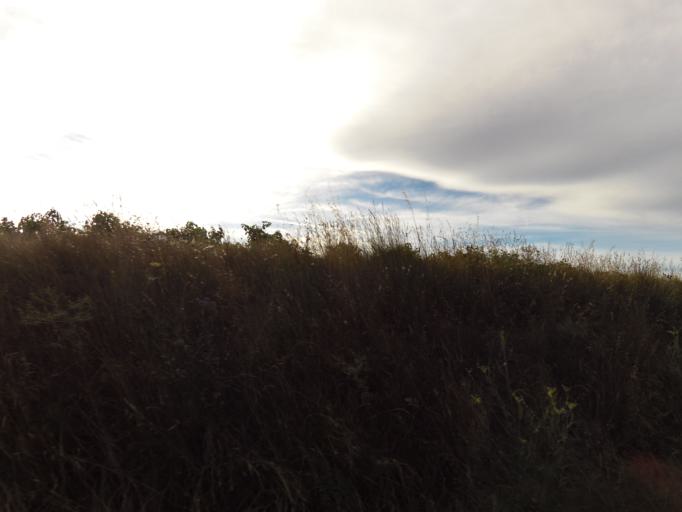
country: FR
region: Languedoc-Roussillon
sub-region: Departement du Gard
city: Saint-Mamert-du-Gard
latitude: 43.8614
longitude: 4.1602
